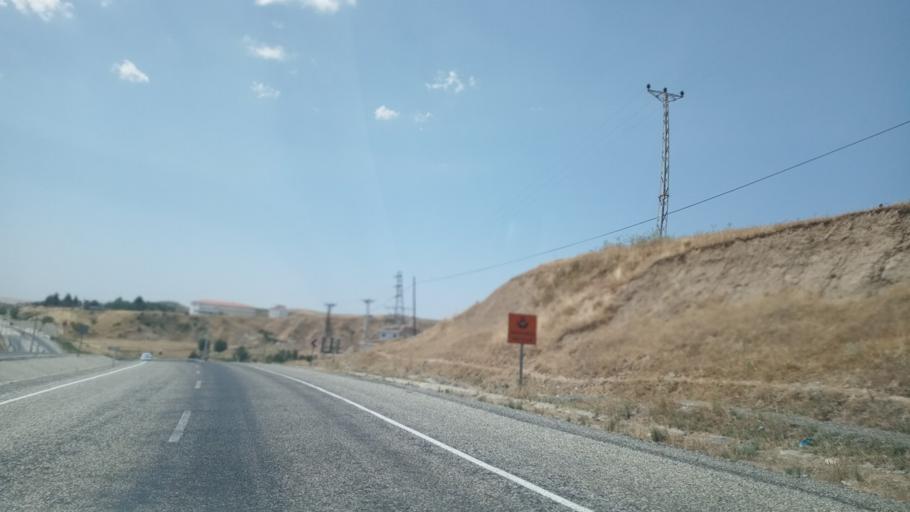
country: TR
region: Batman
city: Bekirhan
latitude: 38.1490
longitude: 41.3019
